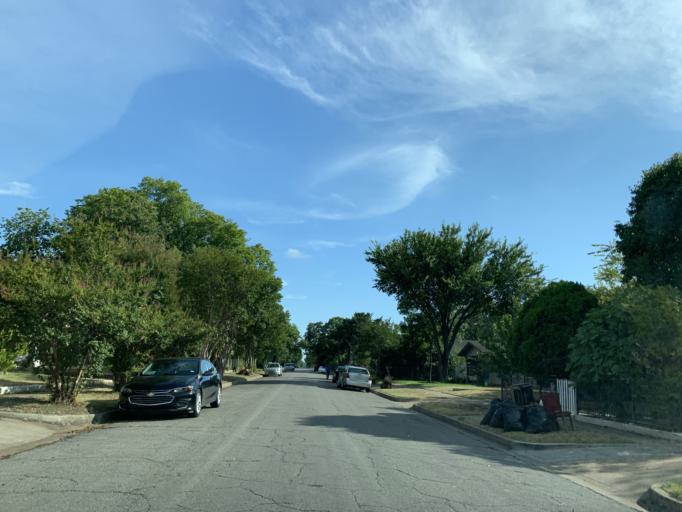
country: US
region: Texas
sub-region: Dallas County
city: Cockrell Hill
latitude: 32.7342
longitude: -96.8517
